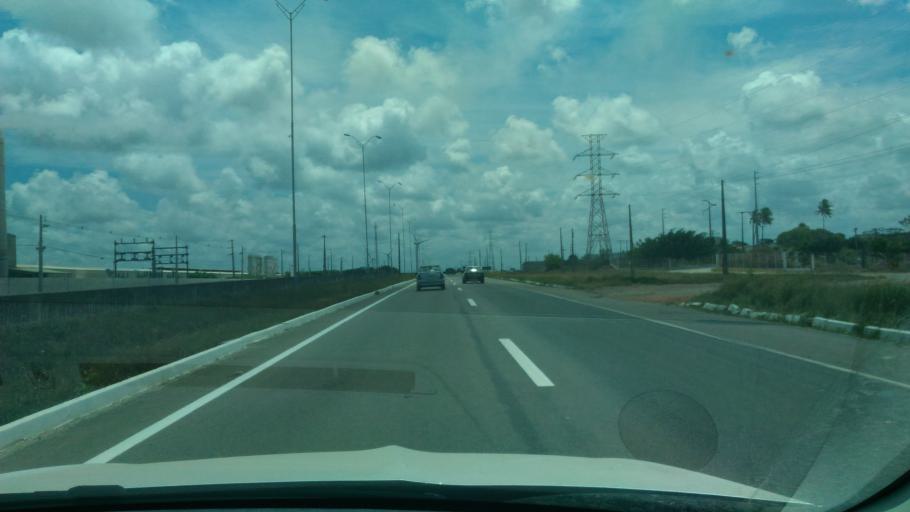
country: BR
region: Paraiba
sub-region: Conde
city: Conde
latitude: -7.2499
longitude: -34.9324
